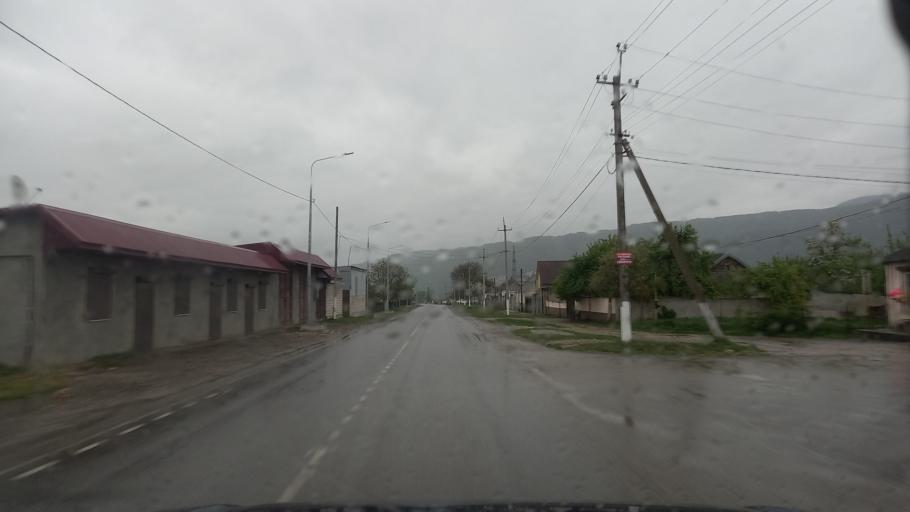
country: RU
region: Kabardino-Balkariya
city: Zhankhoteko
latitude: 43.5885
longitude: 43.2132
